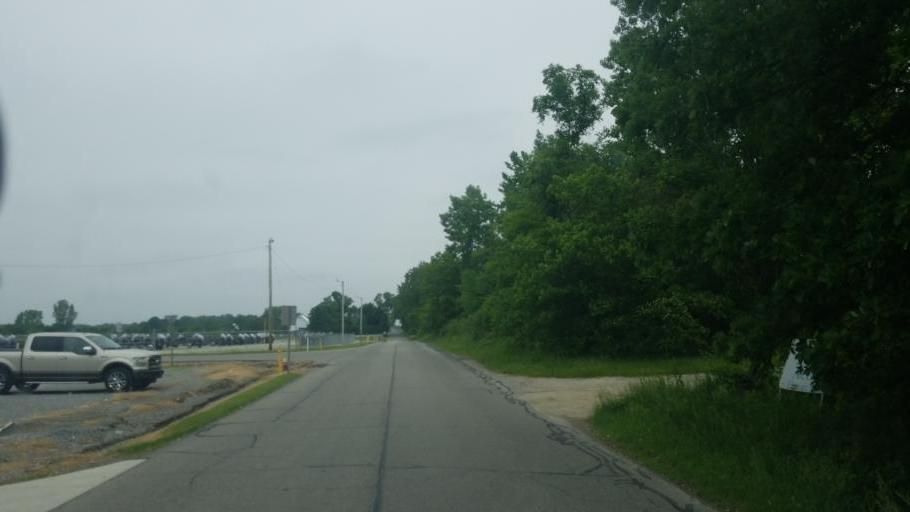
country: US
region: Indiana
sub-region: Elkhart County
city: Nappanee
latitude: 41.4476
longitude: -86.0207
